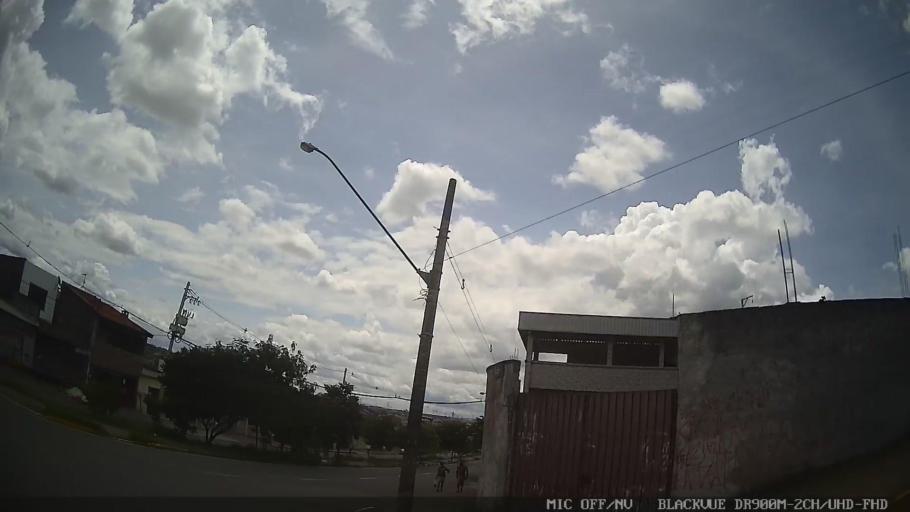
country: BR
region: Sao Paulo
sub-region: Mogi das Cruzes
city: Mogi das Cruzes
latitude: -23.5772
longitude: -46.2219
